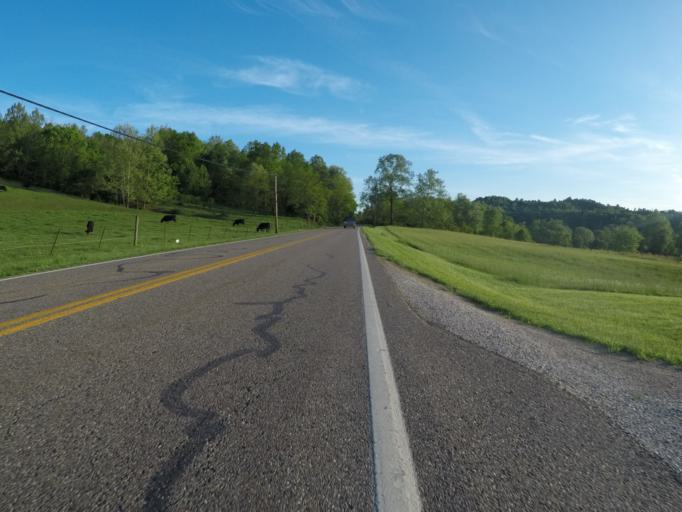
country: US
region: West Virginia
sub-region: Cabell County
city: Huntington
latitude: 38.5197
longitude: -82.4732
